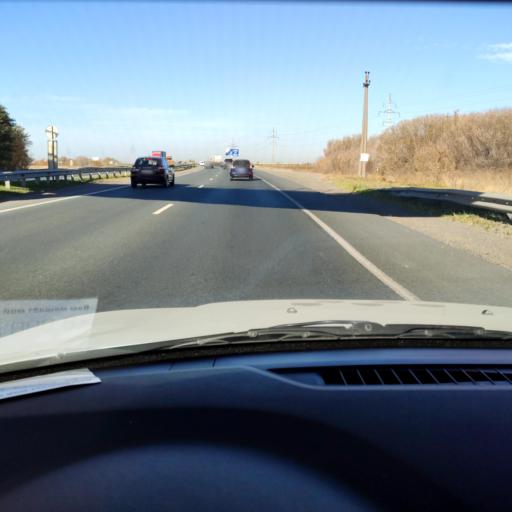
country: RU
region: Samara
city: Tol'yatti
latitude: 53.5628
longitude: 49.4974
